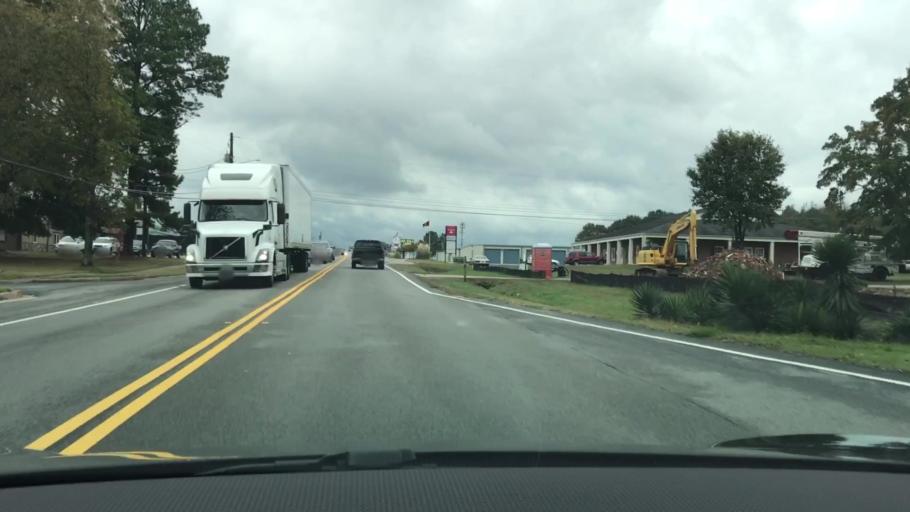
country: US
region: Georgia
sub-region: Oconee County
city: Watkinsville
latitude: 33.8597
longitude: -83.4062
